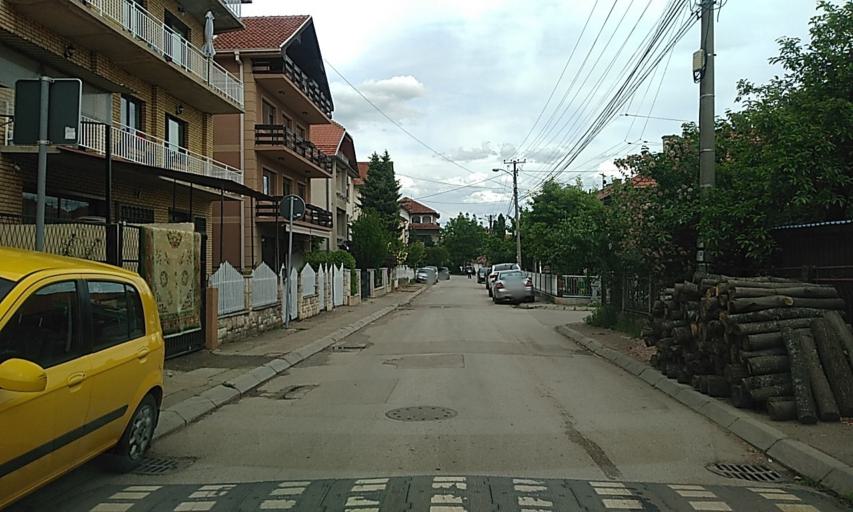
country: RS
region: Central Serbia
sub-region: Nisavski Okrug
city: Nis
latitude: 43.3377
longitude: 21.9108
